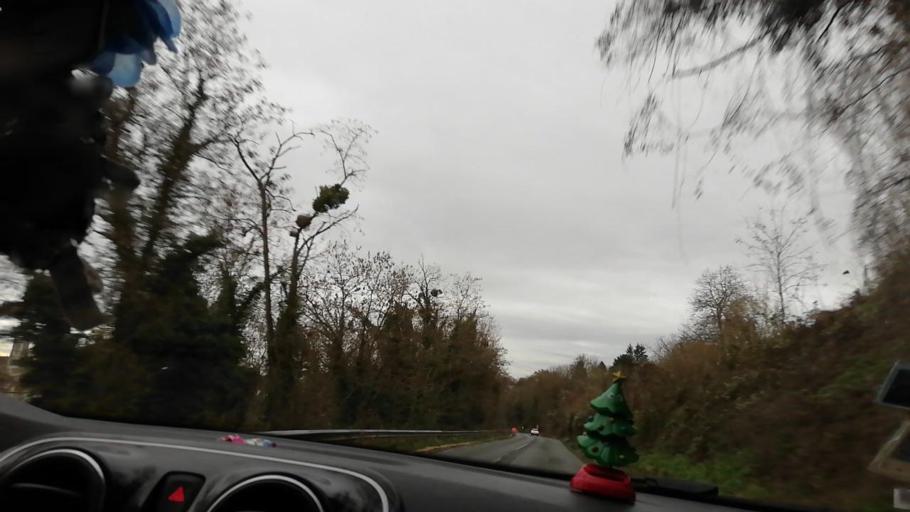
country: FR
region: Ile-de-France
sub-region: Departement de Seine-et-Marne
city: Cregy-les-Meaux
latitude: 48.9682
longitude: 2.8704
